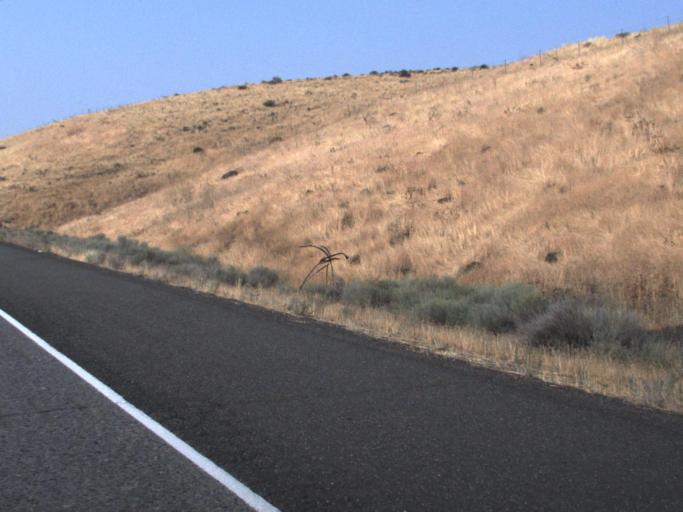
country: US
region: Washington
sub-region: Yakima County
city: Terrace Heights
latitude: 46.7871
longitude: -120.3673
